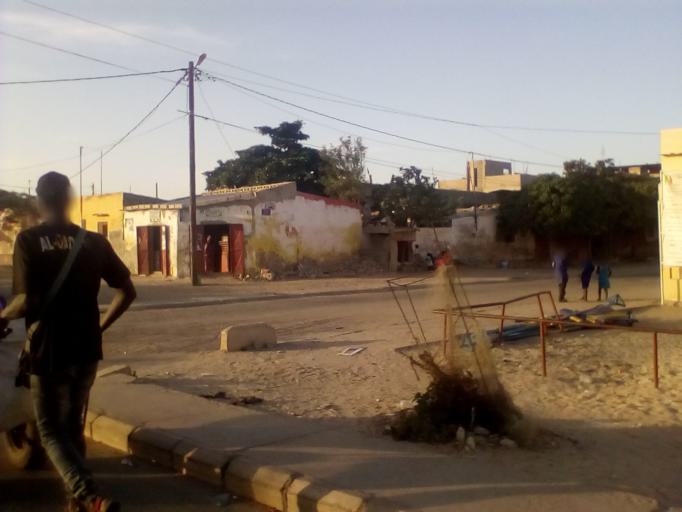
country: SN
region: Saint-Louis
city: Saint-Louis
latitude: 16.0200
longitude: -16.4969
